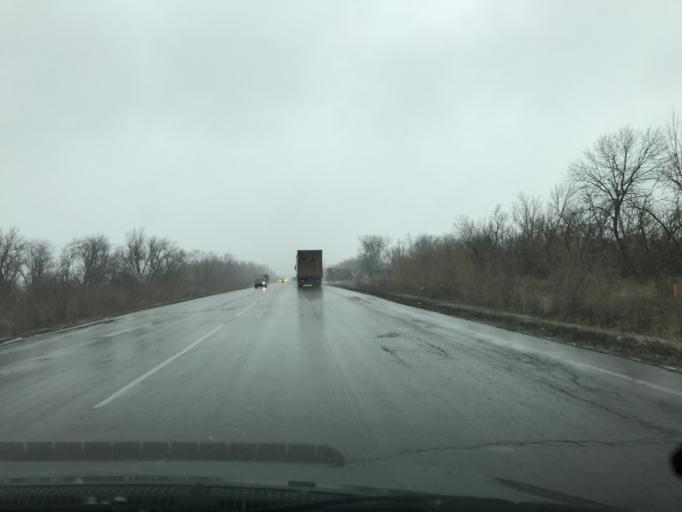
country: RU
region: Rostov
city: Bataysk
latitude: 47.0661
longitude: 39.8053
